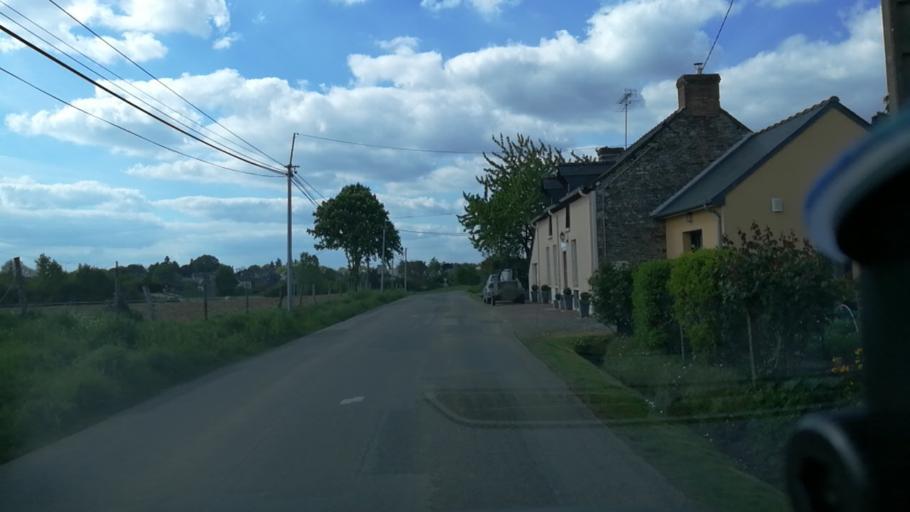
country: FR
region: Brittany
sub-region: Departement d'Ille-et-Vilaine
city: Retiers
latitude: 47.9046
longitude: -1.3712
